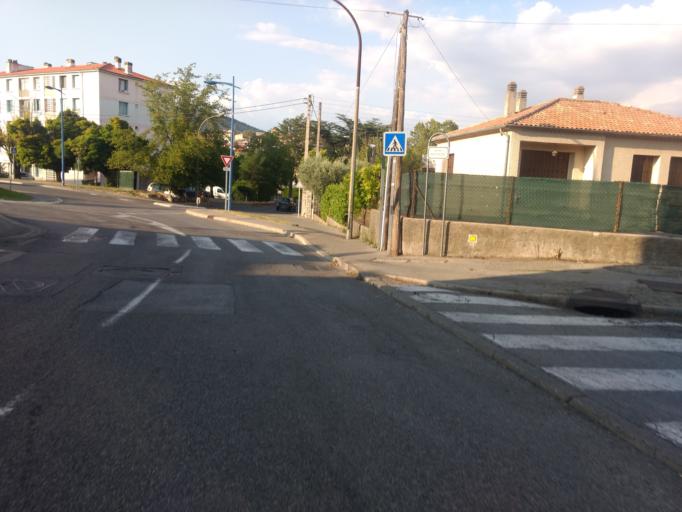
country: FR
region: Provence-Alpes-Cote d'Azur
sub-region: Departement des Alpes-de-Haute-Provence
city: Manosque
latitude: 43.8263
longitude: 5.7809
